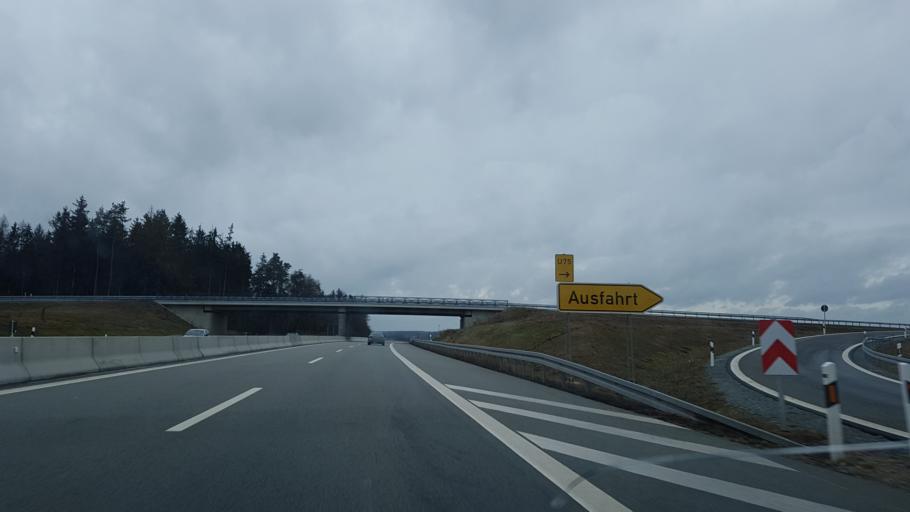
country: DE
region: Bavaria
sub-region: Lower Bavaria
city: Ergoldsbach
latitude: 48.7143
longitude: 12.1694
